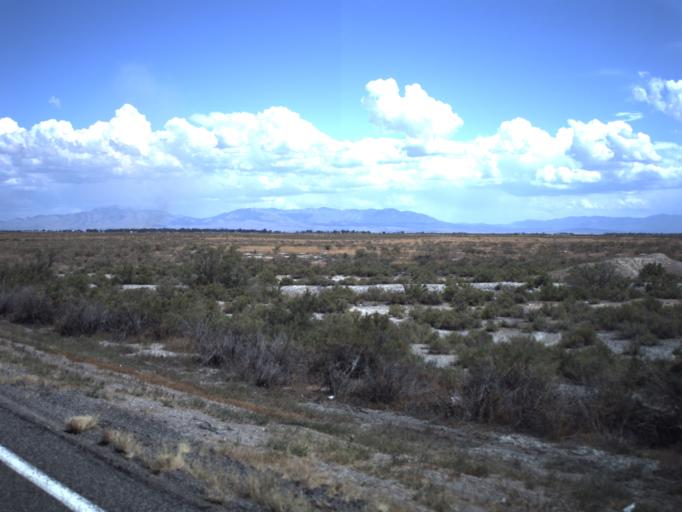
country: US
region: Utah
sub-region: Millard County
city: Delta
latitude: 39.3198
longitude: -112.7421
